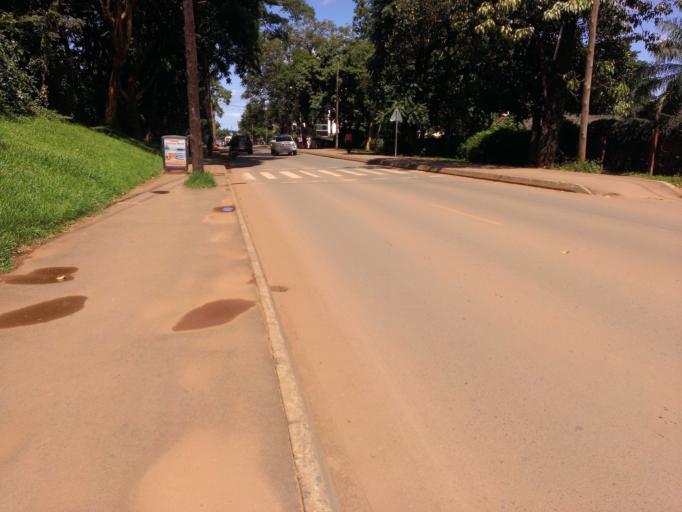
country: UG
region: Central Region
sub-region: Kampala District
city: Kampala
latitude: 0.3190
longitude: 32.5789
